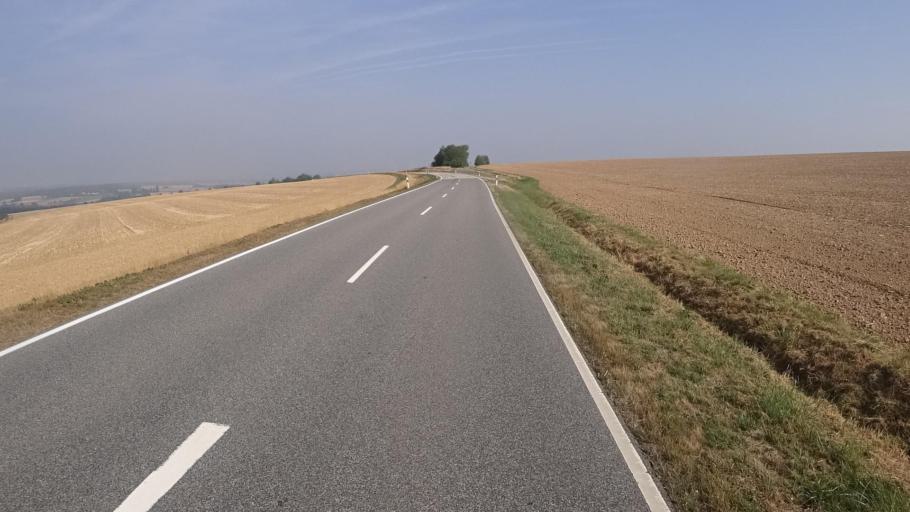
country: DE
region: Rheinland-Pfalz
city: Holzbach
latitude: 49.9620
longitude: 7.5234
